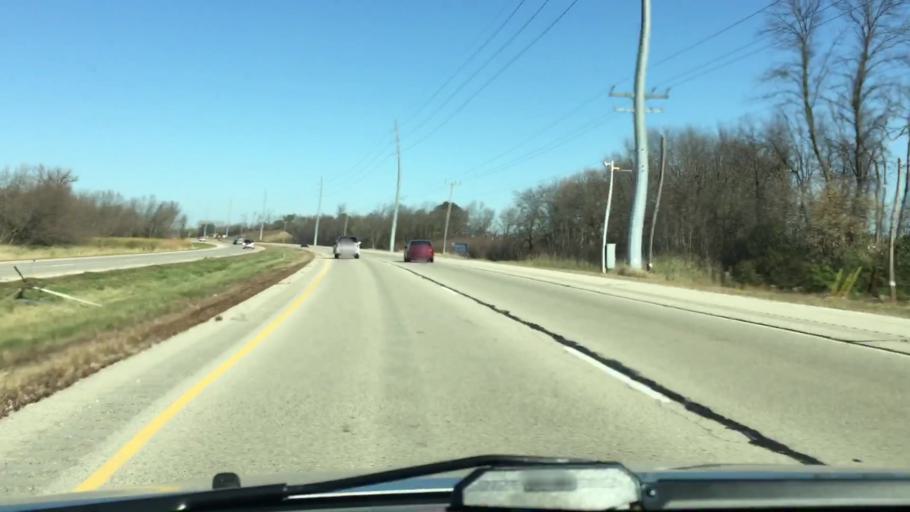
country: US
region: Wisconsin
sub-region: Waukesha County
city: Sussex
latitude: 43.0919
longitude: -88.2053
